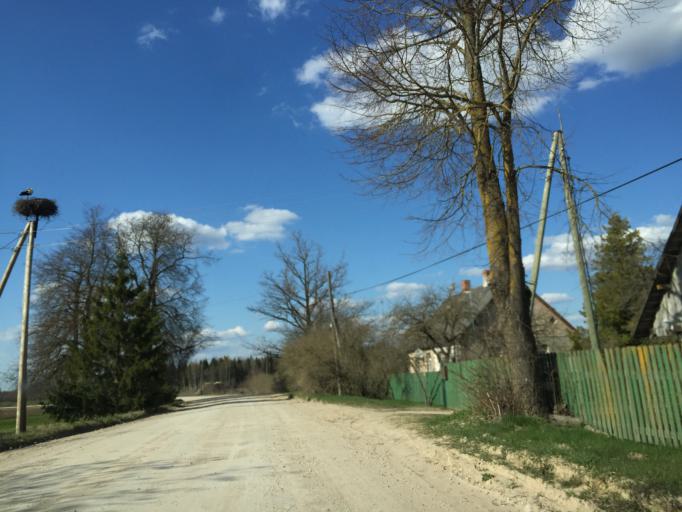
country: LV
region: Saulkrastu
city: Saulkrasti
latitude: 57.3477
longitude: 24.5786
